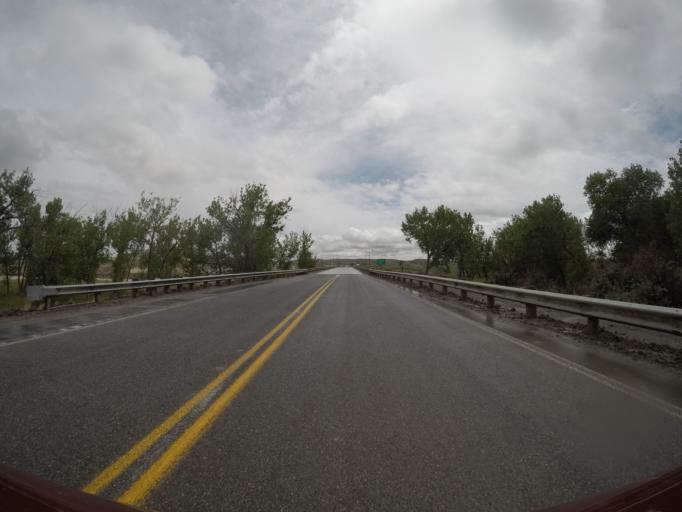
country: US
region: Wyoming
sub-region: Big Horn County
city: Lovell
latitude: 44.8594
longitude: -108.3316
